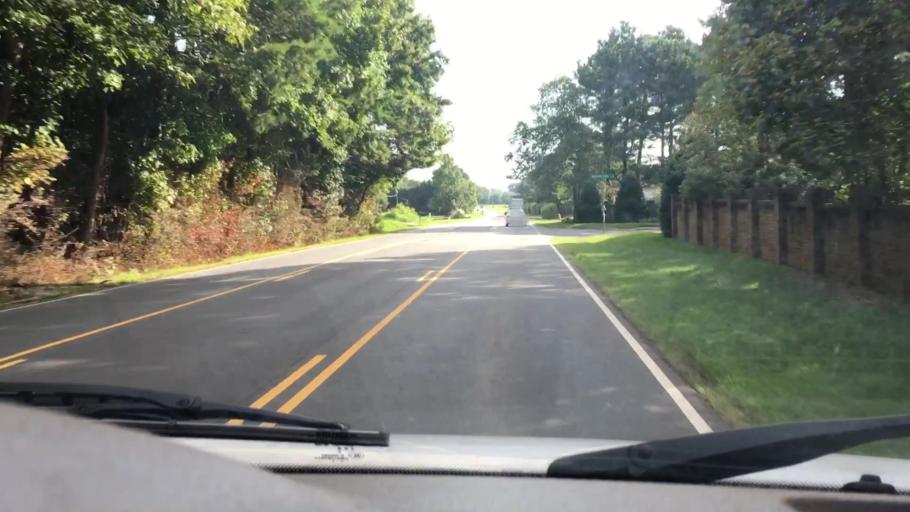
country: US
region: North Carolina
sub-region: Mecklenburg County
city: Huntersville
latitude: 35.3727
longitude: -80.8062
